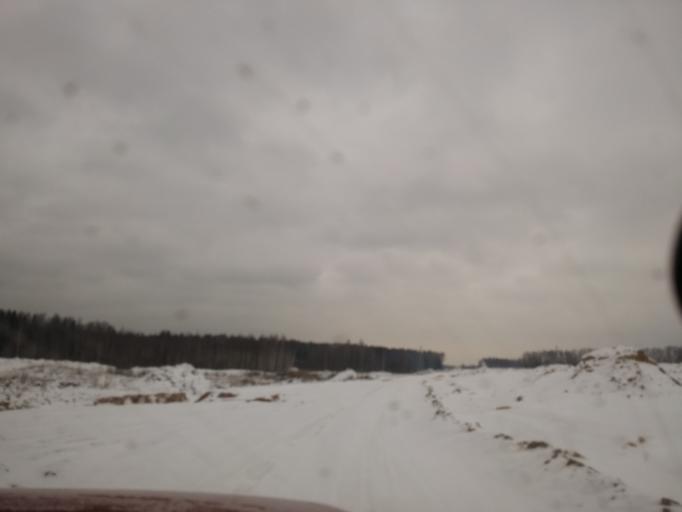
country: RU
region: Moskovskaya
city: Reshetnikovo
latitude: 56.4636
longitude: 36.5408
